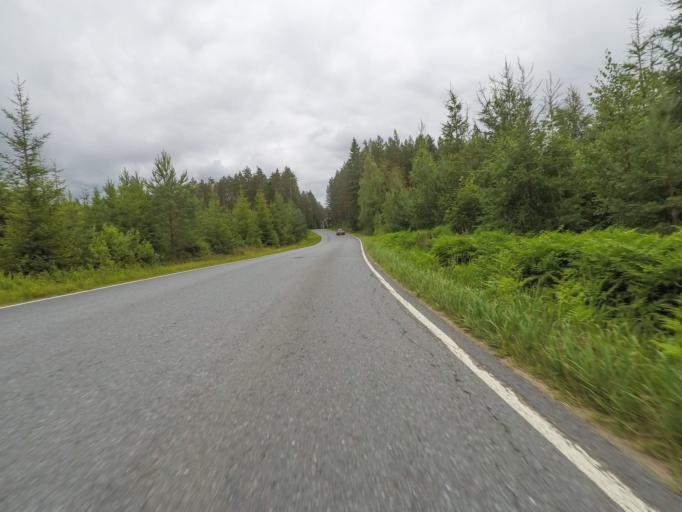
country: FI
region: Varsinais-Suomi
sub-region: Salo
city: Muurla
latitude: 60.3381
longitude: 23.2995
